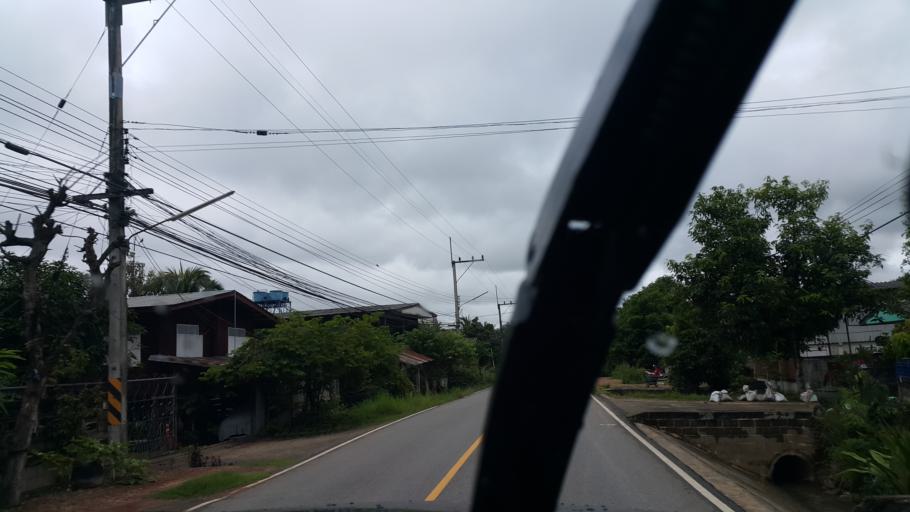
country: TH
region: Phayao
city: Chiang Kham
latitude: 19.5234
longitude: 100.3363
